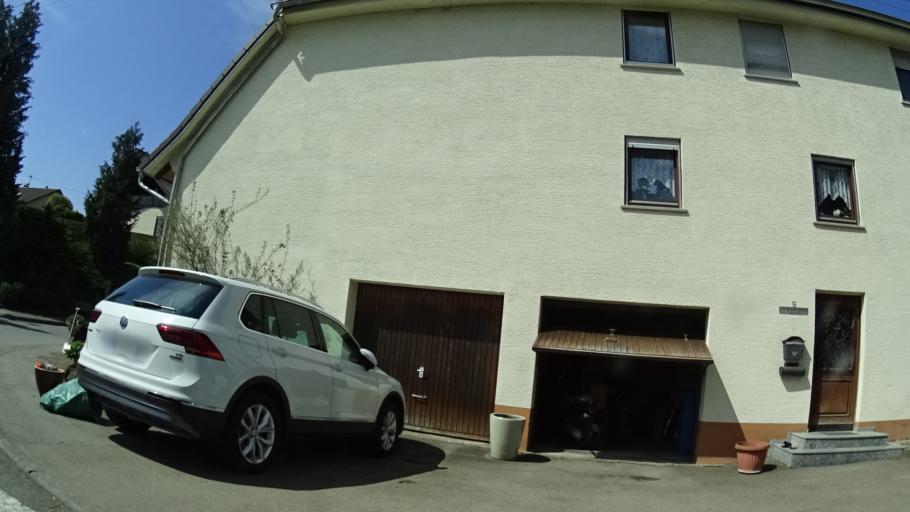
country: DE
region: Baden-Wuerttemberg
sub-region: Freiburg Region
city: Dietingen
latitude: 48.2077
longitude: 8.6491
